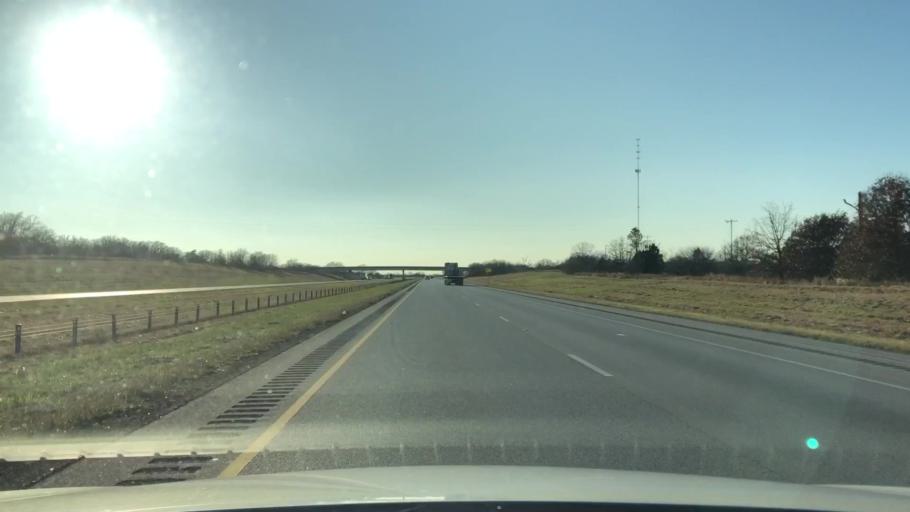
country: US
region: Texas
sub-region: Fayette County
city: Flatonia
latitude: 29.6948
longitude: -97.1539
